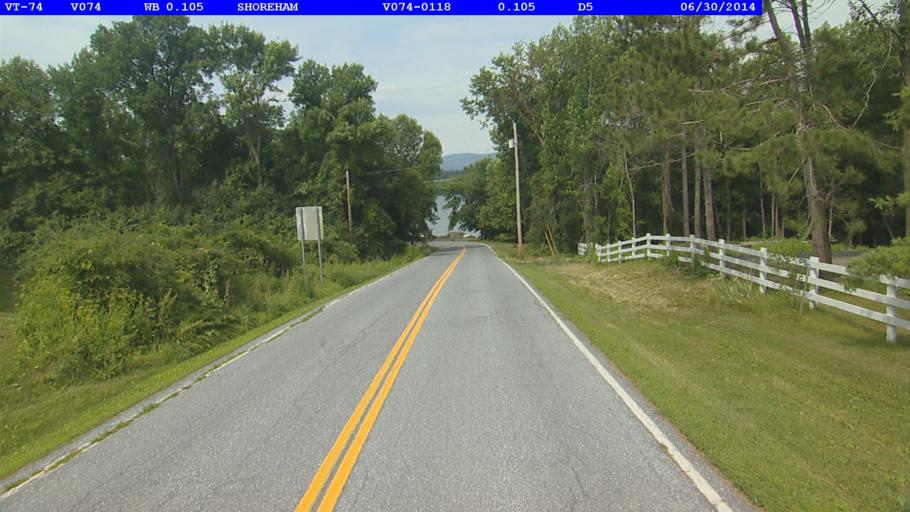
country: US
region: New York
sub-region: Essex County
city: Ticonderoga
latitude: 43.8561
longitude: -73.3748
